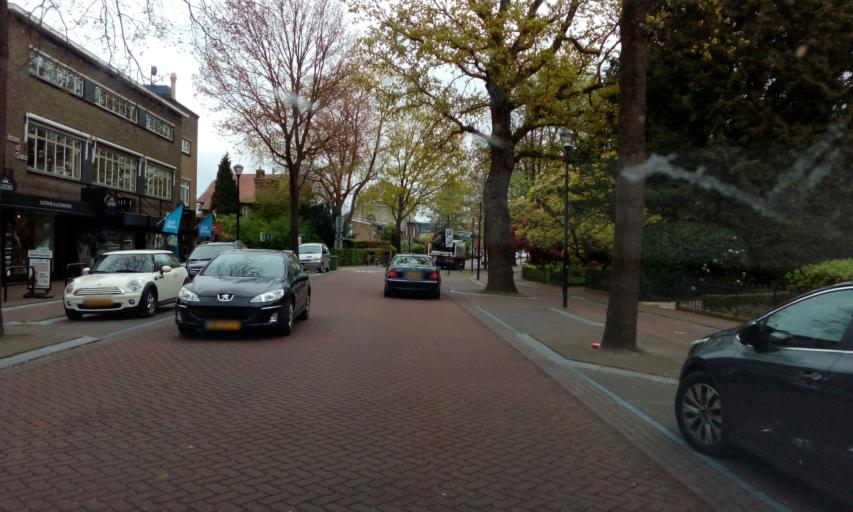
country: NL
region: Utrecht
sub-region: Gemeente Soest
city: Soest
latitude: 52.1838
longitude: 5.3011
